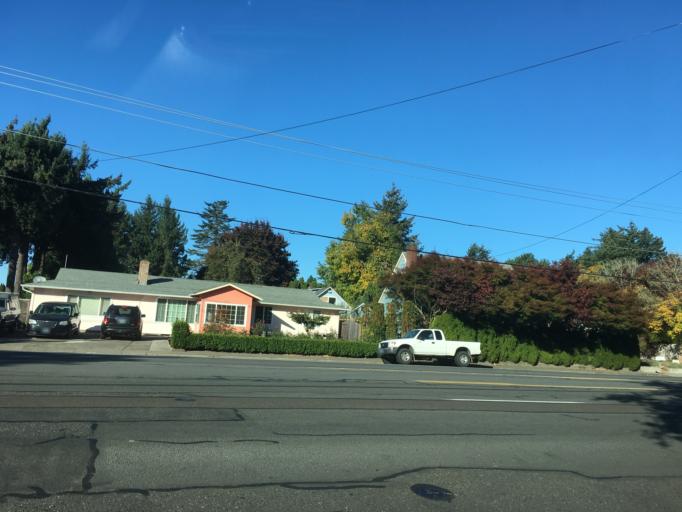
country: US
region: Oregon
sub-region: Multnomah County
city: Gresham
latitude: 45.5047
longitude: -122.4057
